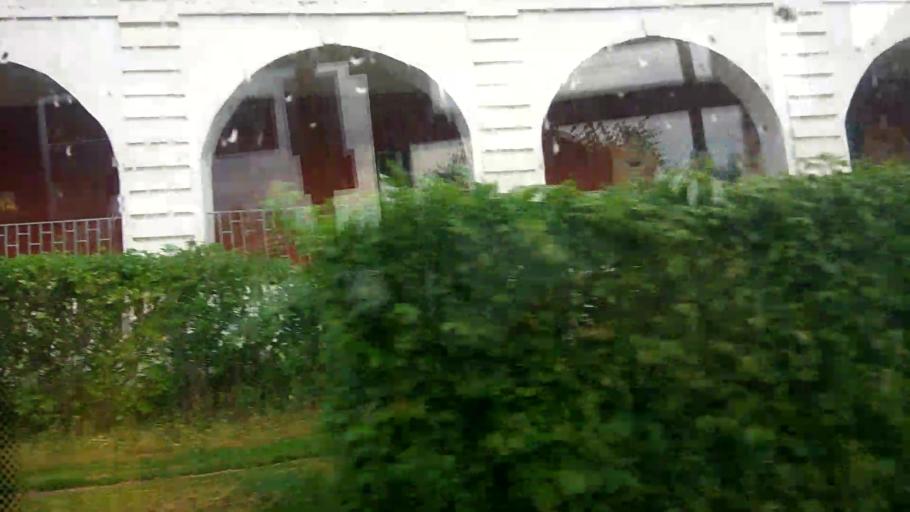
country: RU
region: Moskovskaya
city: Zaraysk
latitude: 54.7578
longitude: 38.8741
